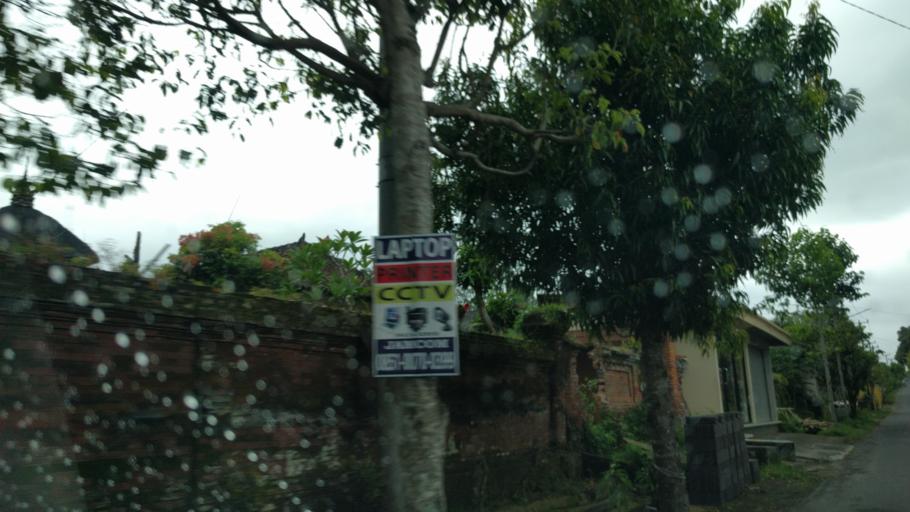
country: ID
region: Bali
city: Banjar Triwangsakeliki
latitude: -8.4536
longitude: 115.2610
